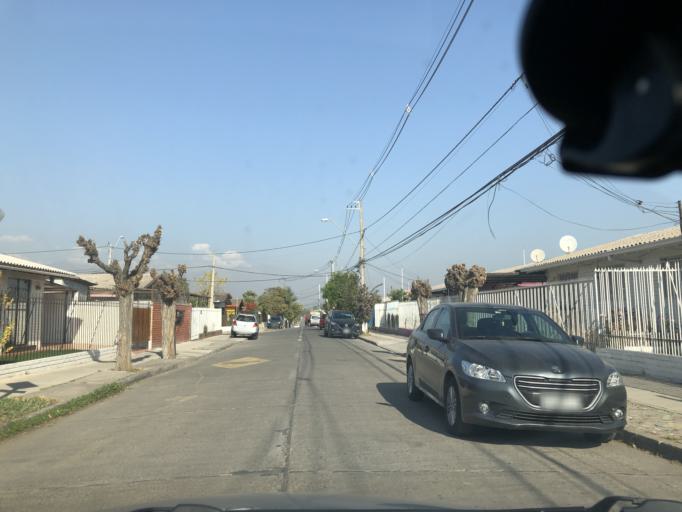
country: CL
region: Santiago Metropolitan
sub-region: Provincia de Cordillera
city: Puente Alto
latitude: -33.6120
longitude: -70.5613
